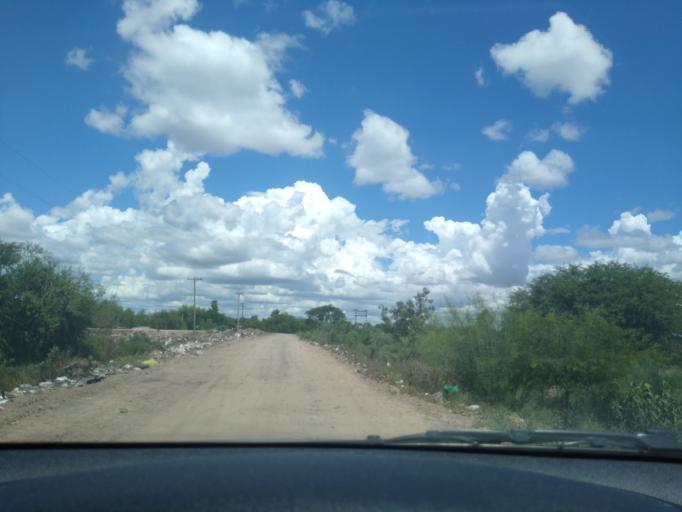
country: AR
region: Chaco
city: Barranqueras
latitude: -27.4693
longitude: -58.9374
